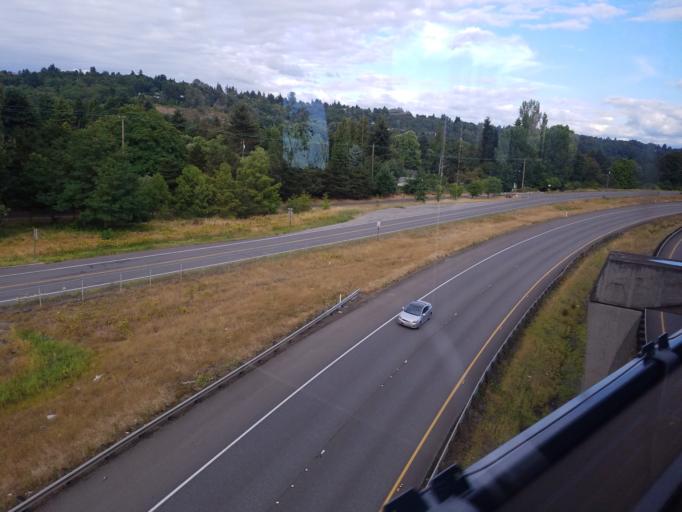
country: US
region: Washington
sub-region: King County
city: Riverton
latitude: 47.4973
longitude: -122.2861
